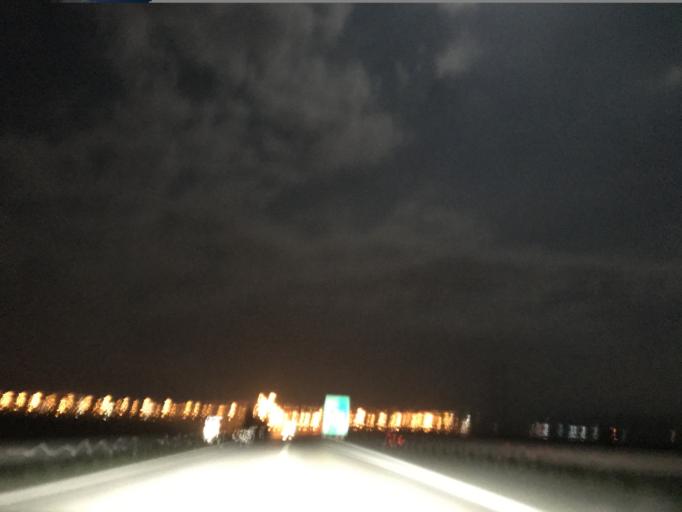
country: TR
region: Hatay
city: Mahmutlar
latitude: 36.9650
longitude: 36.0984
